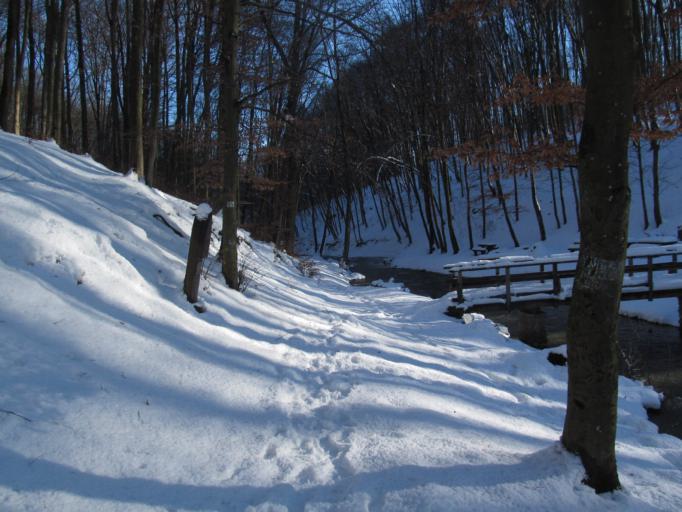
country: HU
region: Veszprem
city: Cseteny
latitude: 47.2715
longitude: 17.9900
